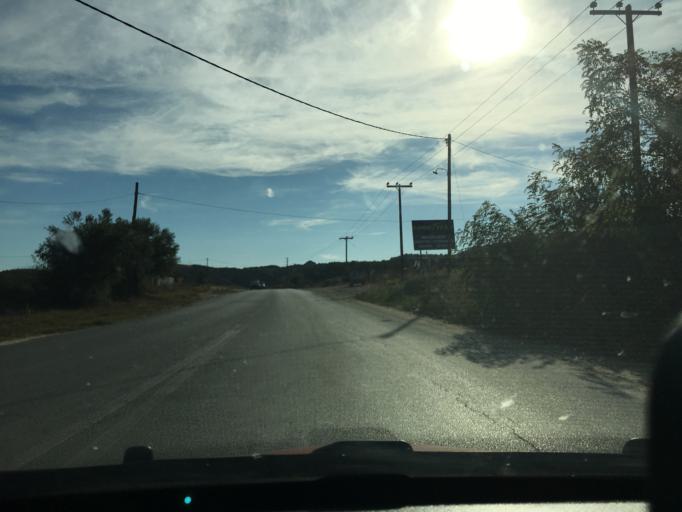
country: GR
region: Central Macedonia
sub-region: Nomos Chalkidikis
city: Agios Nikolaos
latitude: 40.2446
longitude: 23.7082
